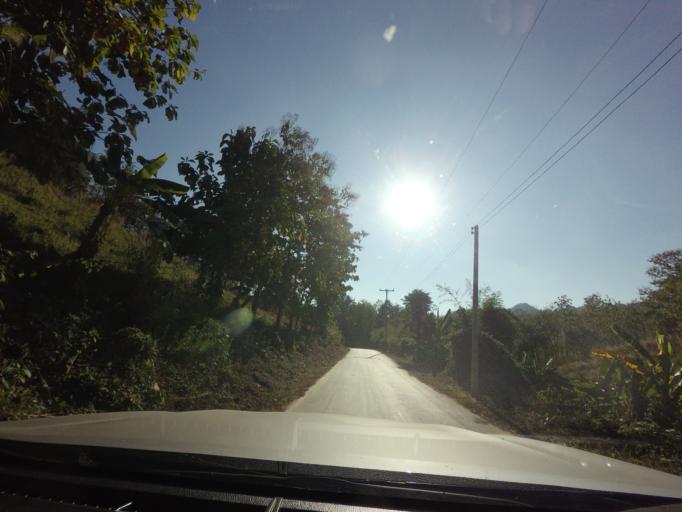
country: TH
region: Lampang
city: Chae Hom
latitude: 18.5992
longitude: 99.6277
